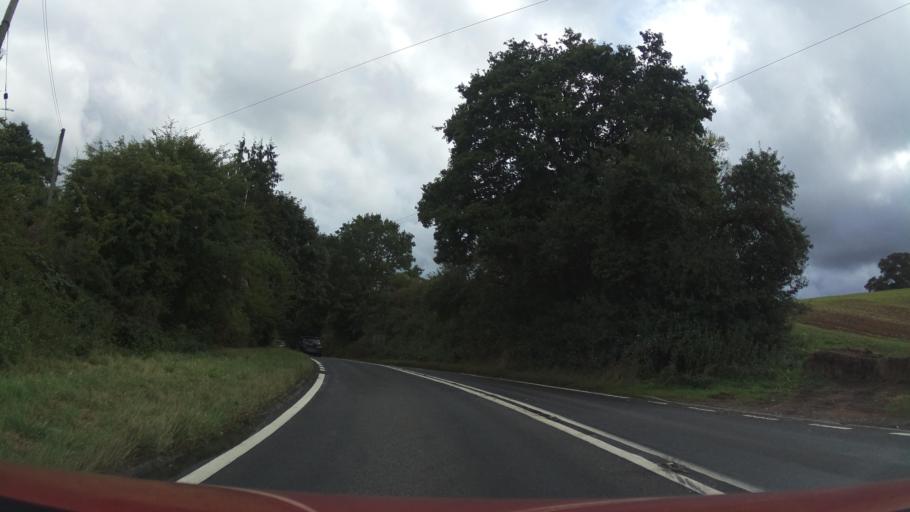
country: GB
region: England
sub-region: Shropshire
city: Bridgnorth
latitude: 52.5634
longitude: -2.3940
